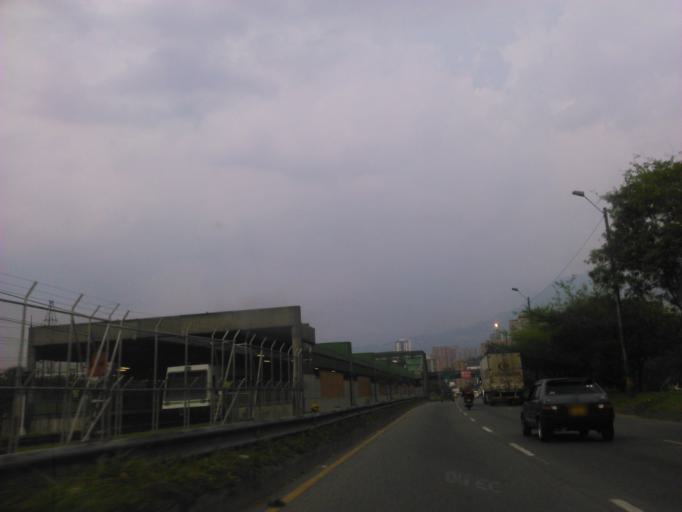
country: CO
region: Antioquia
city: Envigado
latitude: 6.1853
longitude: -75.5869
